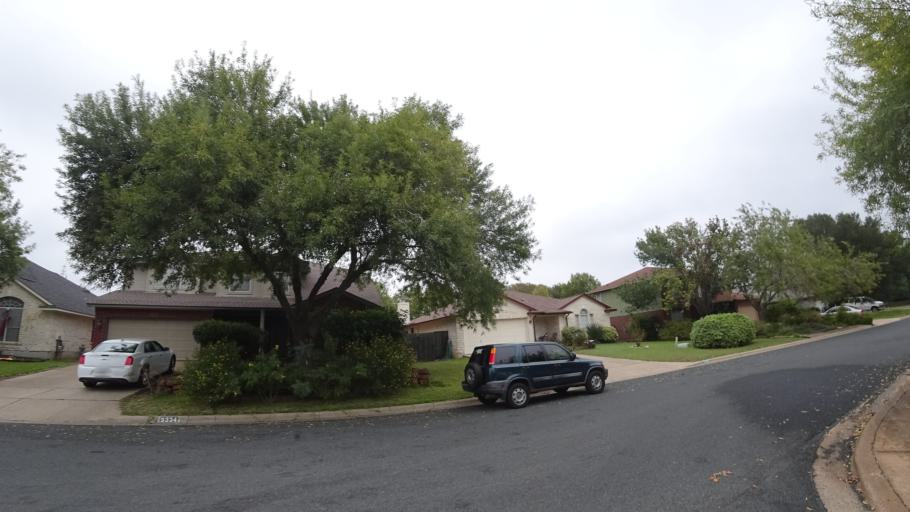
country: US
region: Texas
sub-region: Travis County
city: Shady Hollow
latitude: 30.1888
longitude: -97.8397
